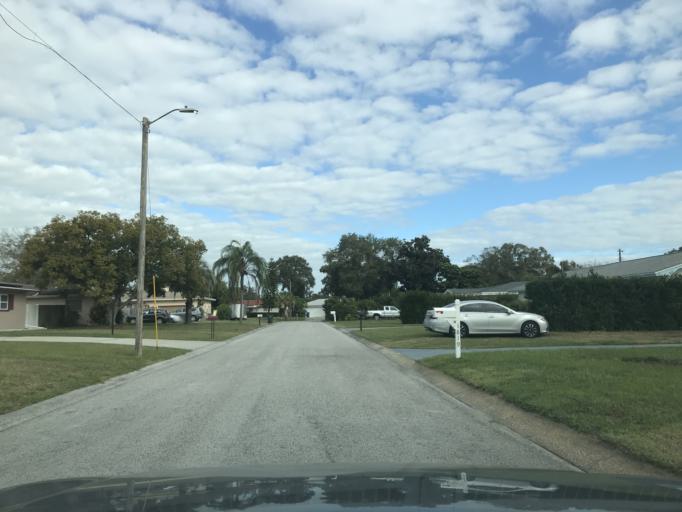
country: US
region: Florida
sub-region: Pinellas County
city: Largo
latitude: 27.9301
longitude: -82.7825
